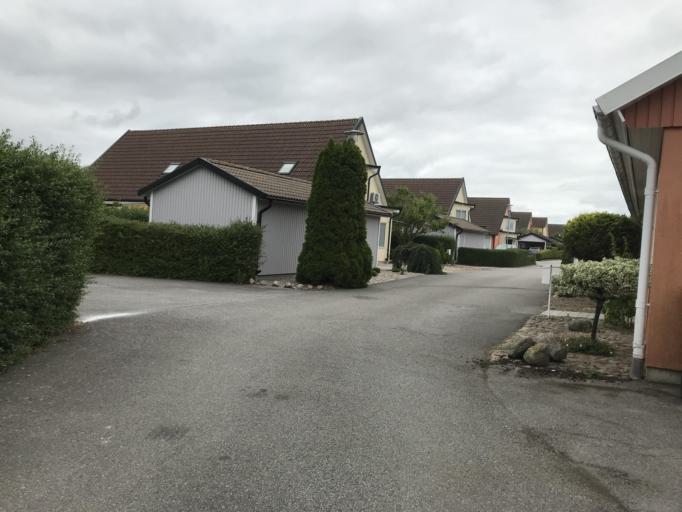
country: SE
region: Skane
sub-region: Burlovs Kommun
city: Arloev
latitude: 55.6354
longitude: 13.0612
